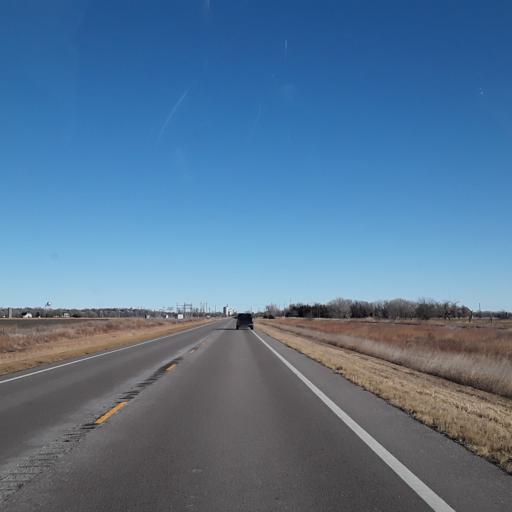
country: US
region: Kansas
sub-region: Pawnee County
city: Larned
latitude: 38.1556
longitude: -99.1278
